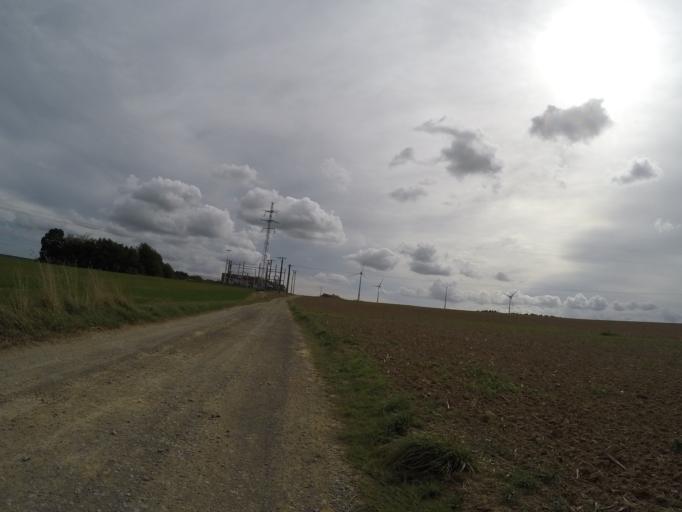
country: BE
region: Wallonia
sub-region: Province de Namur
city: Assesse
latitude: 50.3075
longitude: 4.9793
